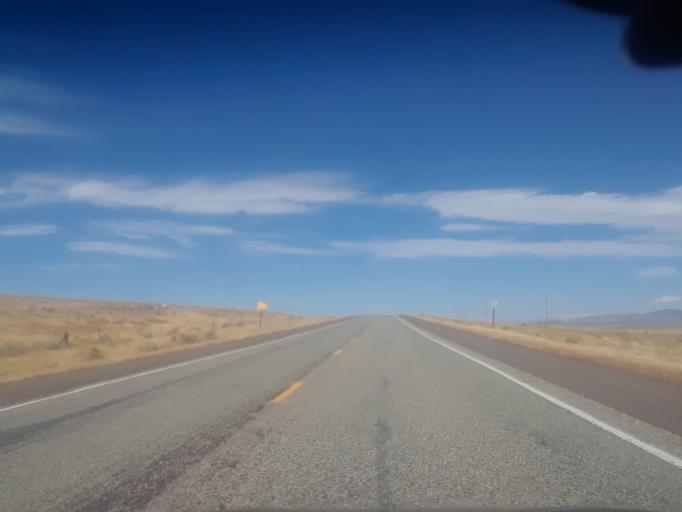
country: US
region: Colorado
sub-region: Conejos County
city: Conejos
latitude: 36.8533
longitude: -105.9719
